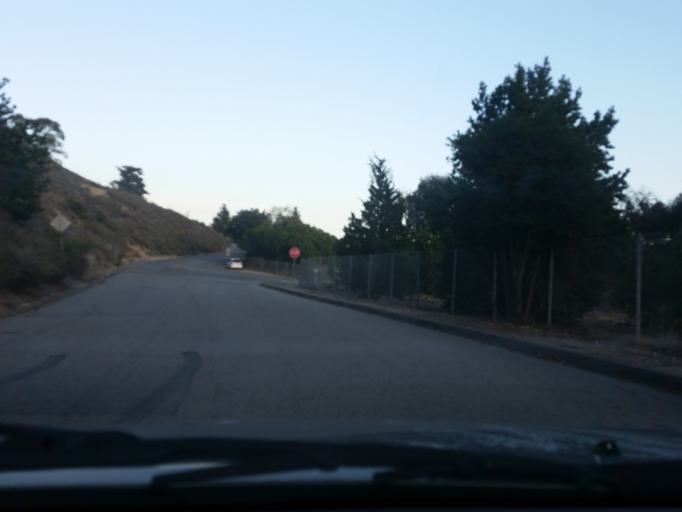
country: US
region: California
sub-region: San Luis Obispo County
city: Avila Beach
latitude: 35.1650
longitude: -120.6875
